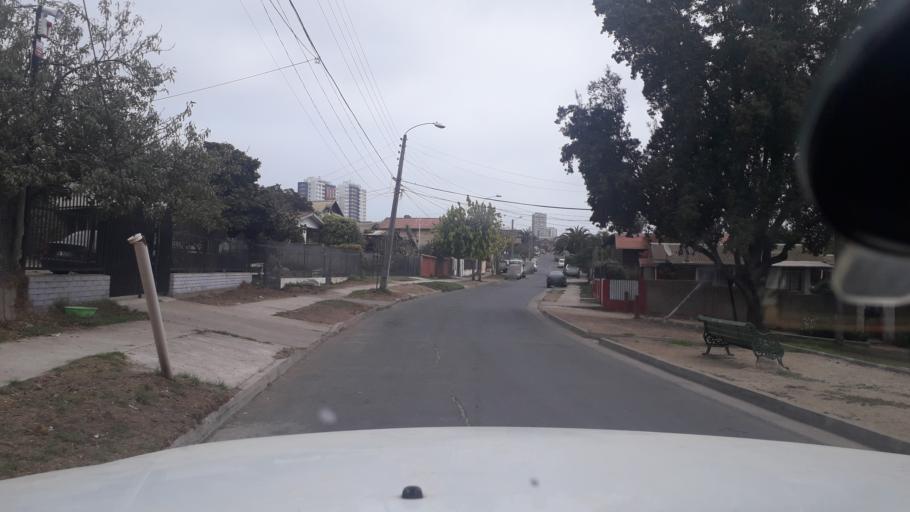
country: CL
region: Valparaiso
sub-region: Provincia de Valparaiso
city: Vina del Mar
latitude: -32.9356
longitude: -71.5249
